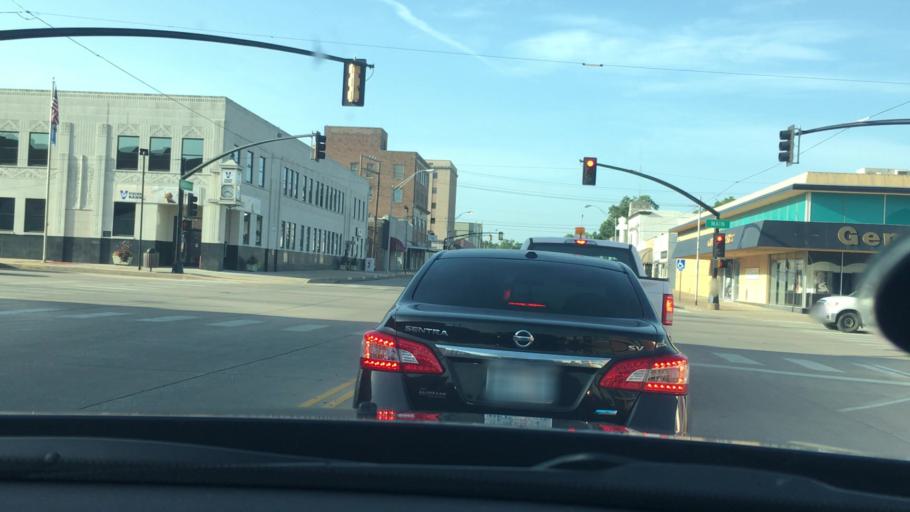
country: US
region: Oklahoma
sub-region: Pontotoc County
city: Ada
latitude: 34.7748
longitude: -96.6787
